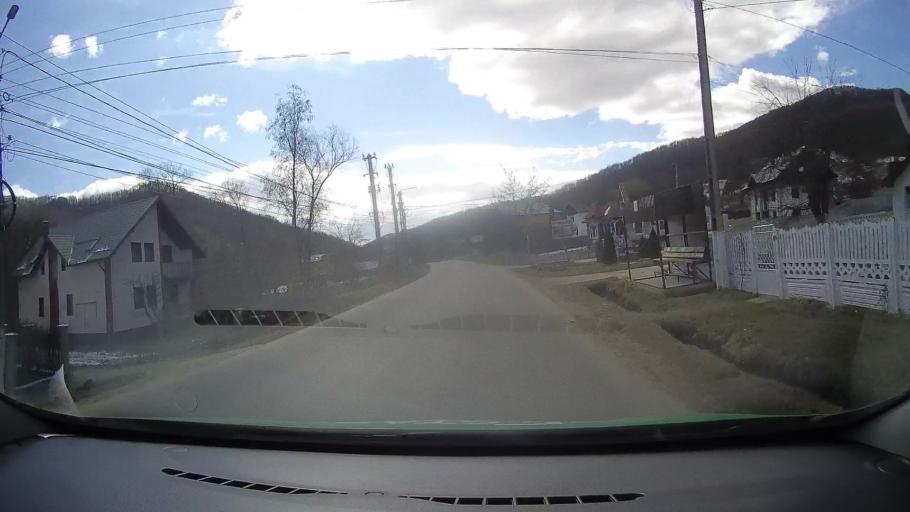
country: RO
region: Dambovita
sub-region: Comuna Vulcana Bai
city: Vulcana Bai
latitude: 45.0663
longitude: 25.3780
